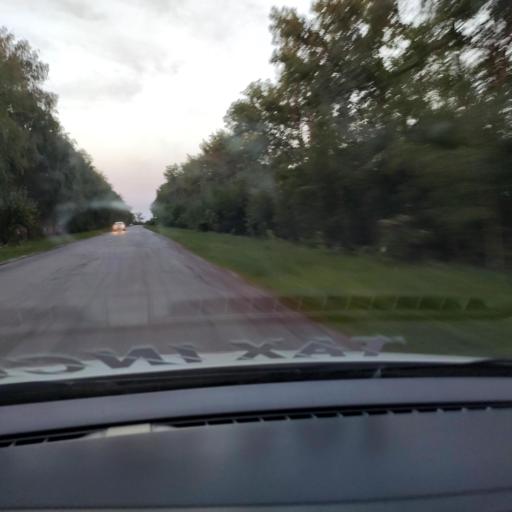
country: RU
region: Voronezj
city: Maslovka
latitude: 51.4383
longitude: 39.2942
